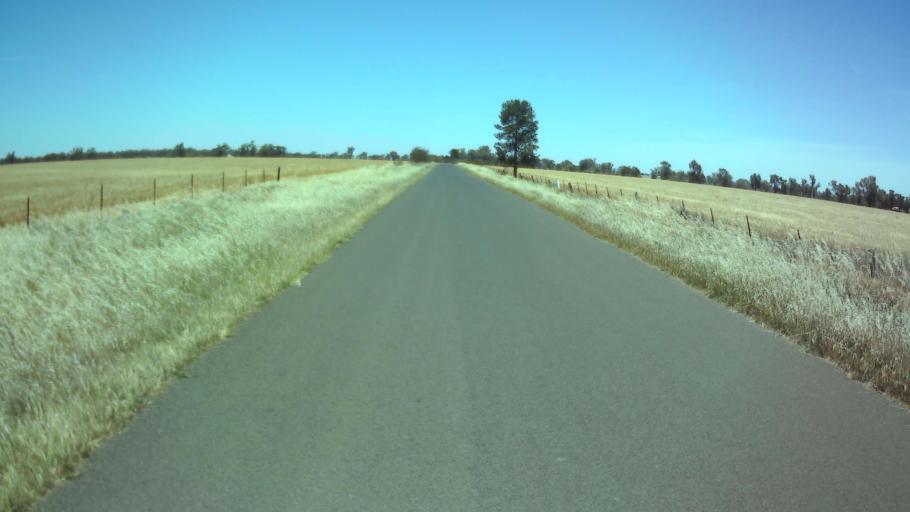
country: AU
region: New South Wales
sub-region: Weddin
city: Grenfell
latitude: -34.0522
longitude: 147.7814
